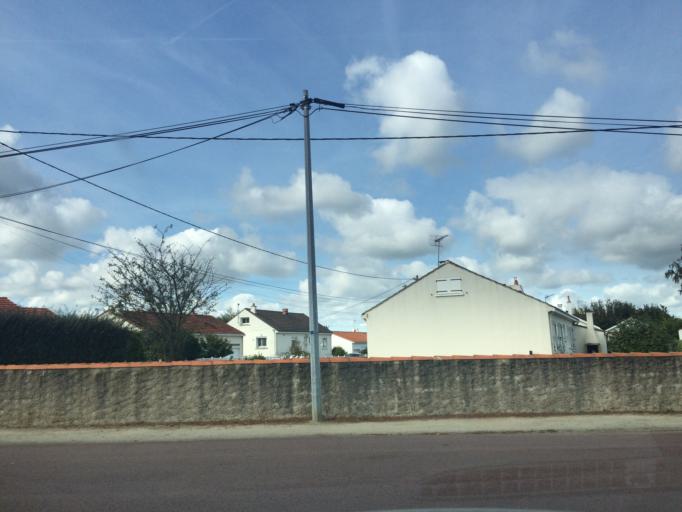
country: FR
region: Pays de la Loire
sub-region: Departement de la Loire-Atlantique
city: Chemere
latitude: 47.1187
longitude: -1.9179
